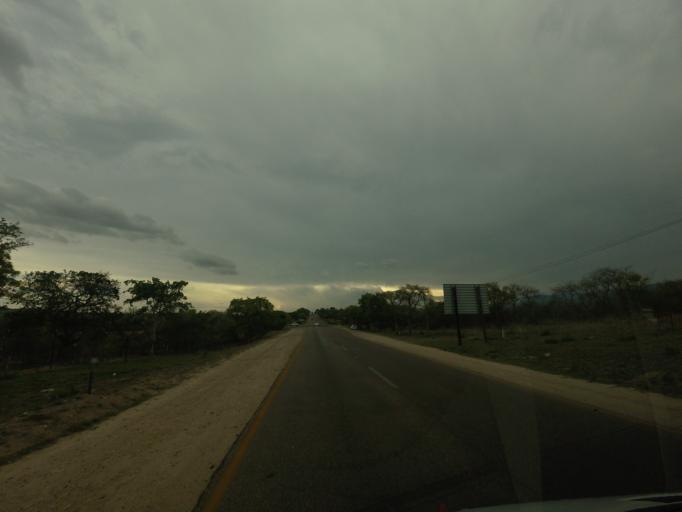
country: ZA
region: Limpopo
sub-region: Mopani District Municipality
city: Hoedspruit
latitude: -24.5535
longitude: 31.0385
